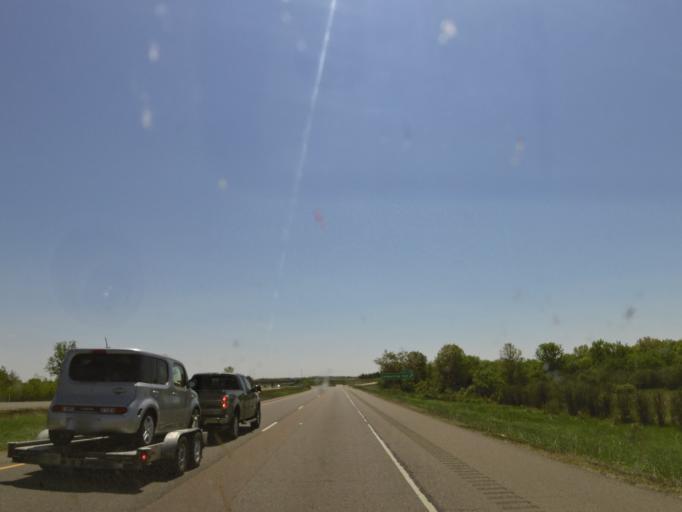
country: US
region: Wisconsin
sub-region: Monroe County
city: Tomah
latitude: 44.0019
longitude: -90.4777
